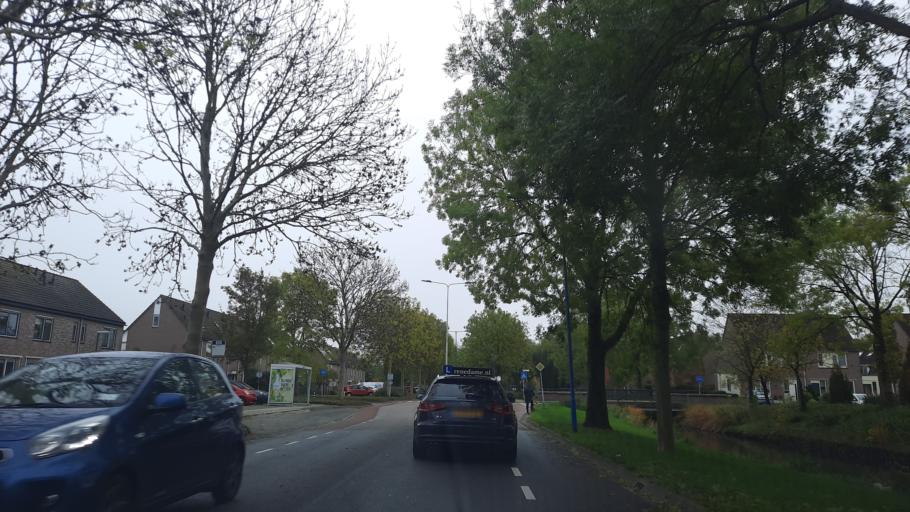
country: NL
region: South Holland
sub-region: Gemeente Gorinchem
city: Gorinchem
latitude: 51.8338
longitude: 4.9922
